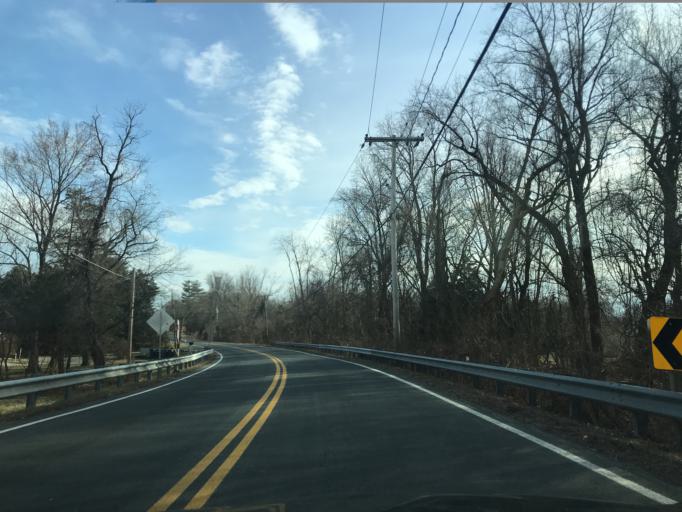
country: US
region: Maryland
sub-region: Prince George's County
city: Woodmore
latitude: 38.9275
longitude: -76.8069
